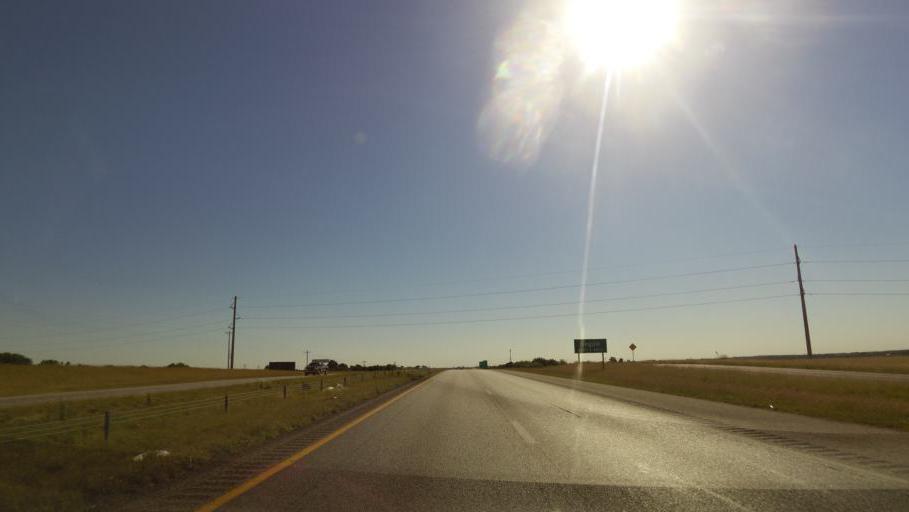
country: US
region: Texas
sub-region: Guadalupe County
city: McQueeney
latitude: 29.5450
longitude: -98.0584
